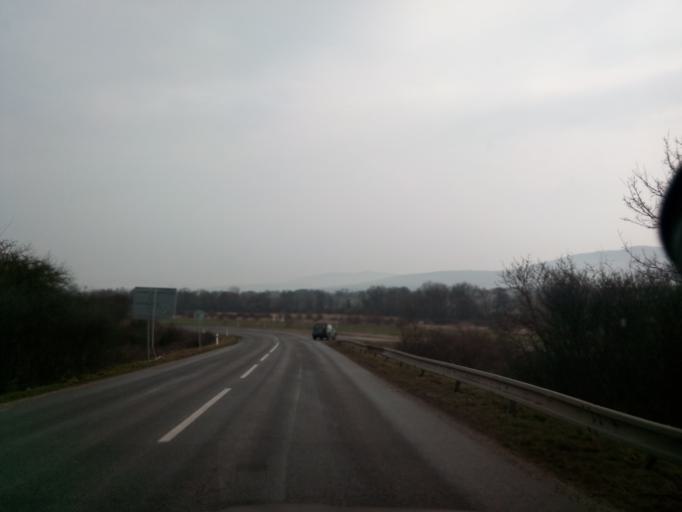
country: SK
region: Kosicky
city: Kosice
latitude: 48.6427
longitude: 21.3725
